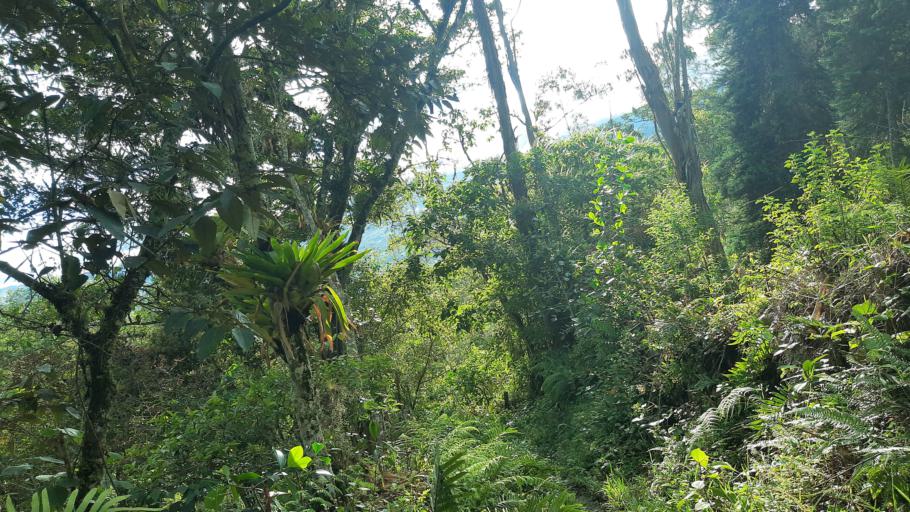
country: CO
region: Boyaca
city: Garagoa
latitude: 5.0943
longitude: -73.3543
